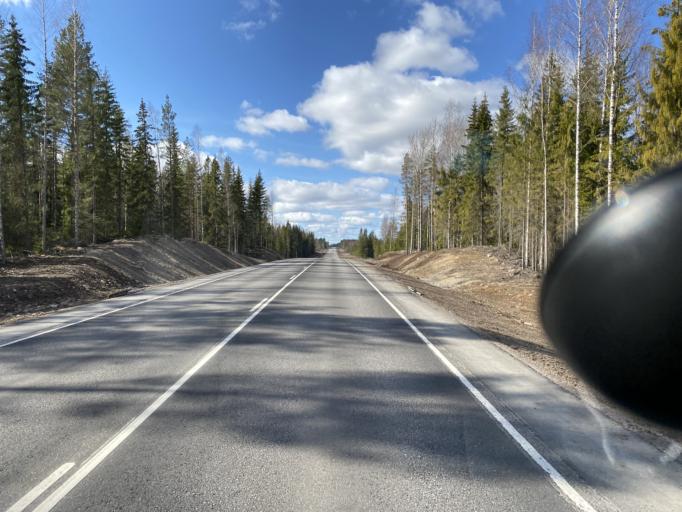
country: FI
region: Satakunta
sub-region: Pori
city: Kokemaeki
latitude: 61.1723
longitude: 22.5033
